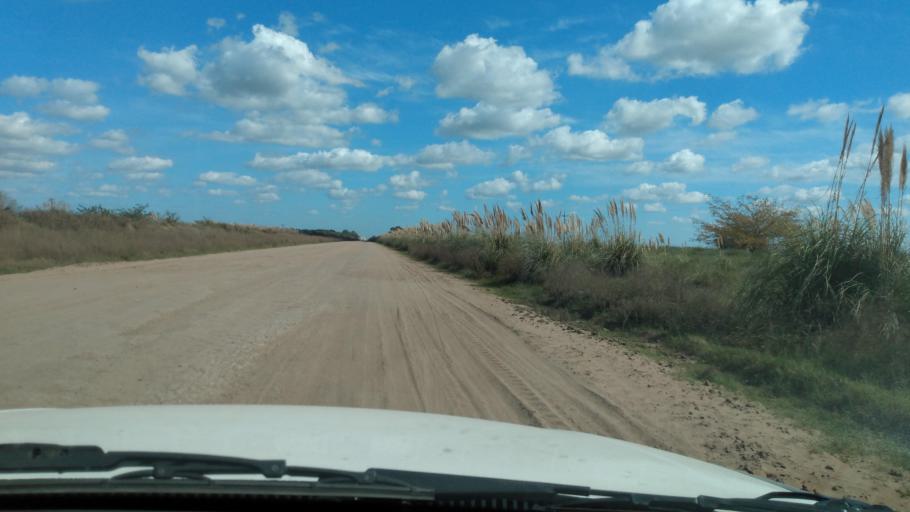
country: AR
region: Buenos Aires
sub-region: Partido de Navarro
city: Navarro
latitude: -35.0038
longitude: -59.3672
